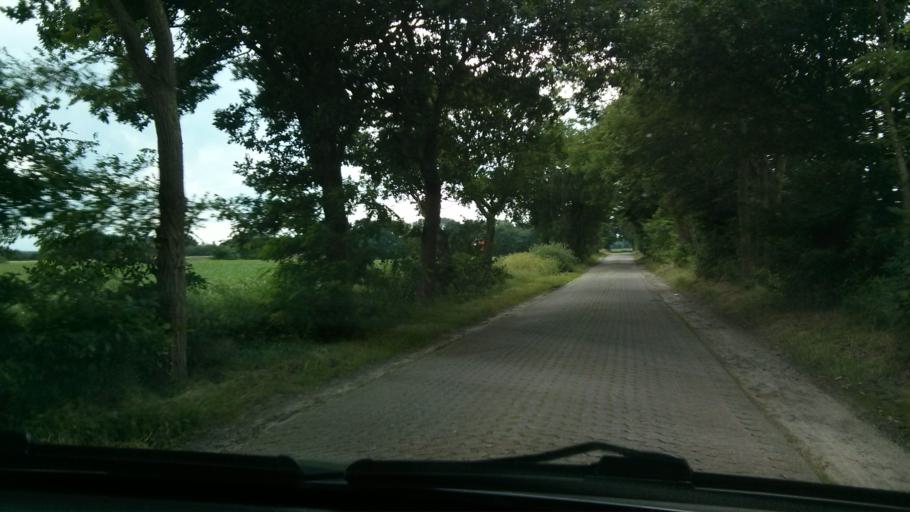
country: DE
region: Lower Saxony
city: Loxstedt
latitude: 53.4999
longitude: 8.6898
